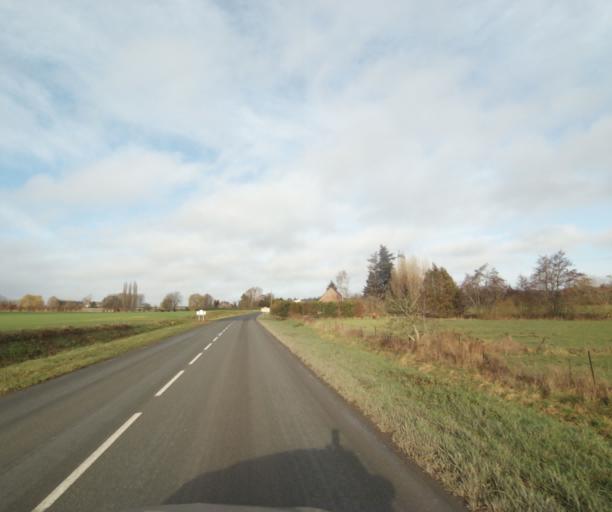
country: FR
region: Nord-Pas-de-Calais
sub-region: Departement du Nord
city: Thiant
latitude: 50.2794
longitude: 3.4530
